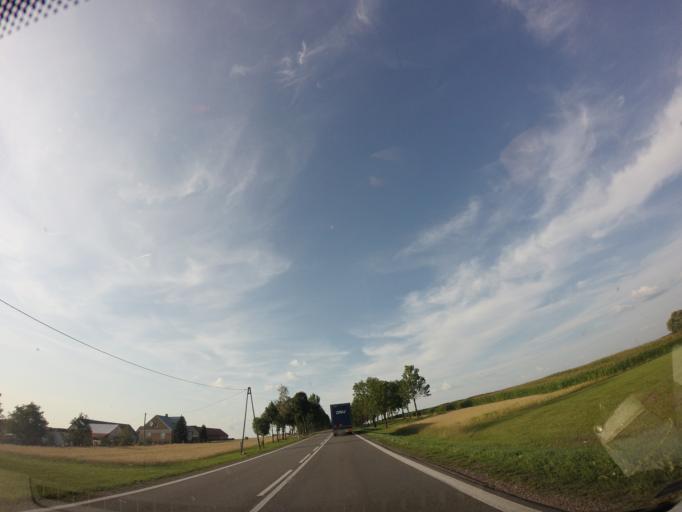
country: PL
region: Podlasie
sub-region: Powiat sokolski
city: Suchowola
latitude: 53.5201
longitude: 23.1056
